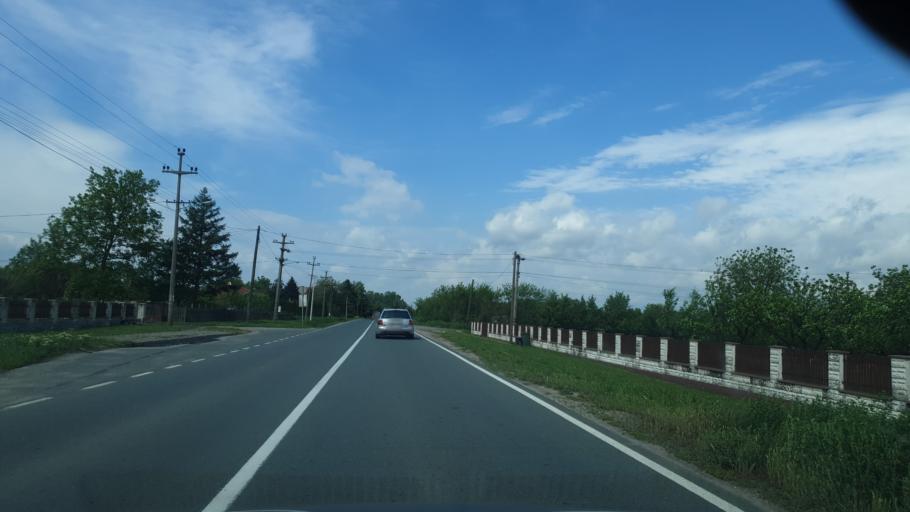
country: RS
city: Stubline
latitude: 44.6008
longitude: 20.1482
